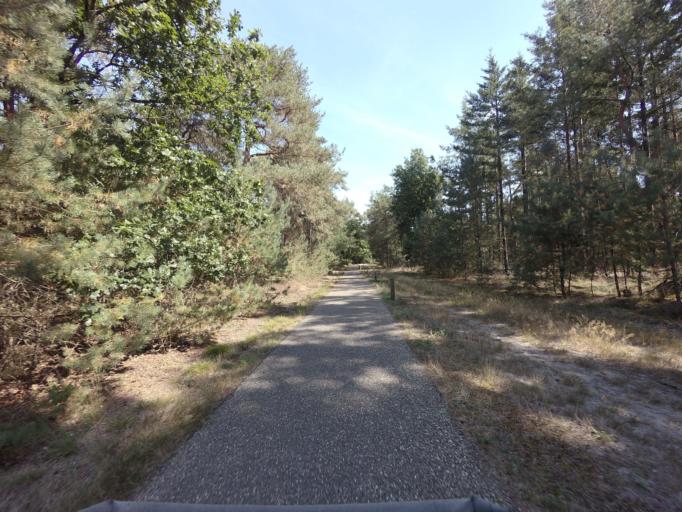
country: NL
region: North Brabant
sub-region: Gemeente Someren
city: Someren
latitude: 51.3630
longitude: 5.6603
